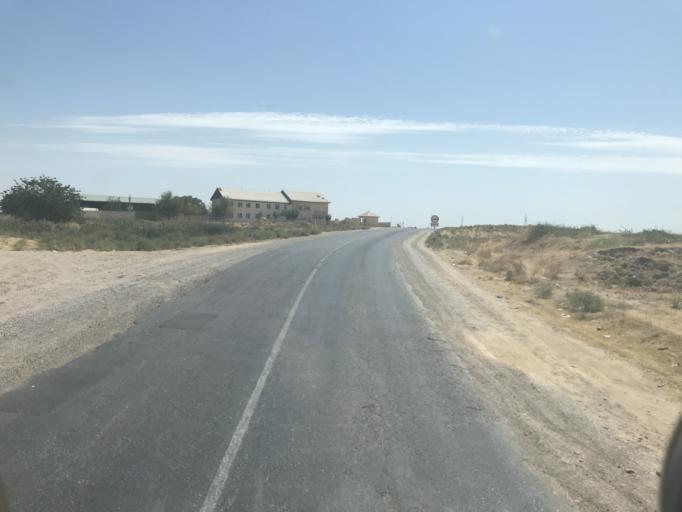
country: UZ
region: Toshkent
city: Yangiyul
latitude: 41.3353
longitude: 68.8854
